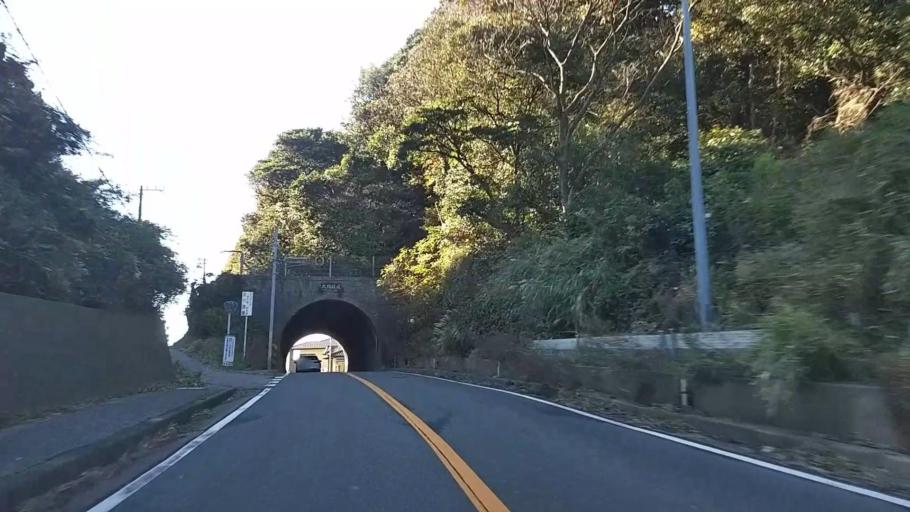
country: JP
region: Chiba
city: Futtsu
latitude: 35.1720
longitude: 139.8183
